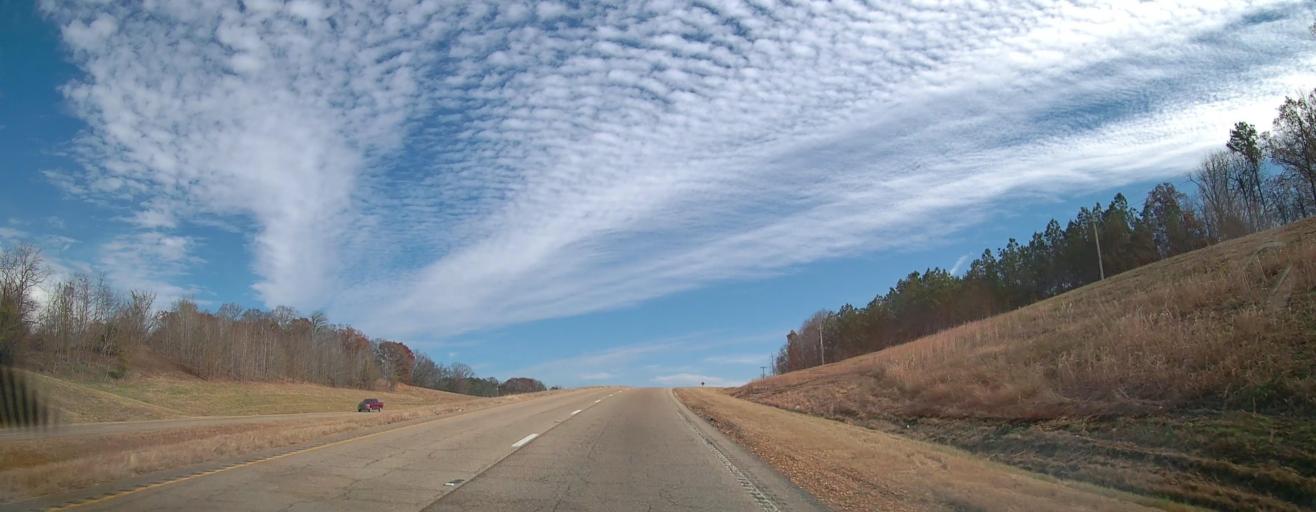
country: US
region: Mississippi
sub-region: Alcorn County
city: Corinth
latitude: 34.9323
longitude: -88.6487
